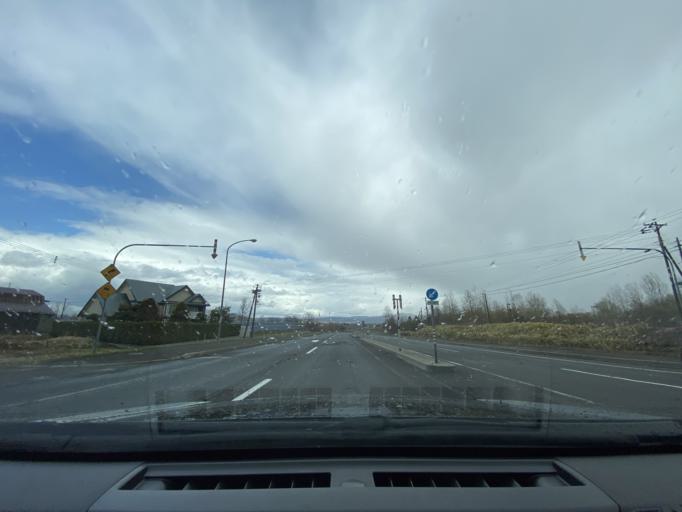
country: JP
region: Hokkaido
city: Fukagawa
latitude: 43.6925
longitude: 142.0570
